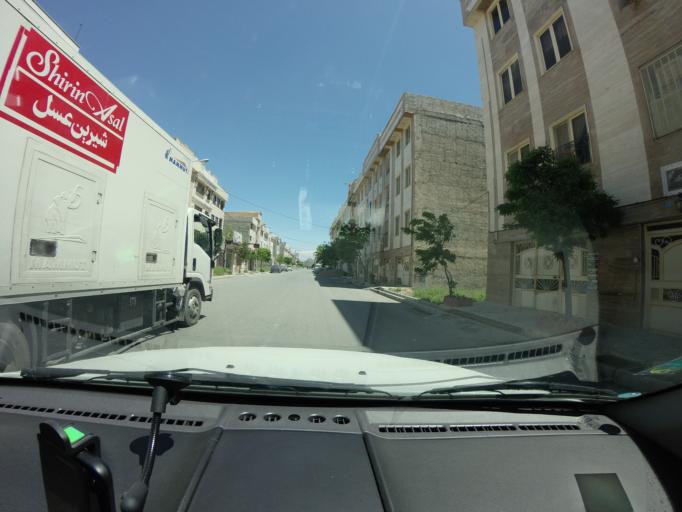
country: IR
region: Tehran
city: Eslamshahr
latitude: 35.5320
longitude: 51.2122
